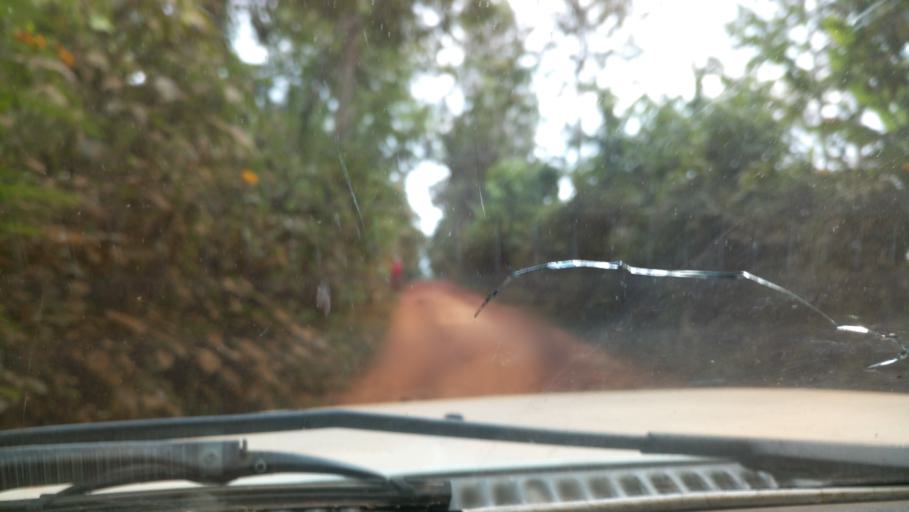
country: KE
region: Murang'a District
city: Maragua
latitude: -0.7781
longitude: 37.1062
